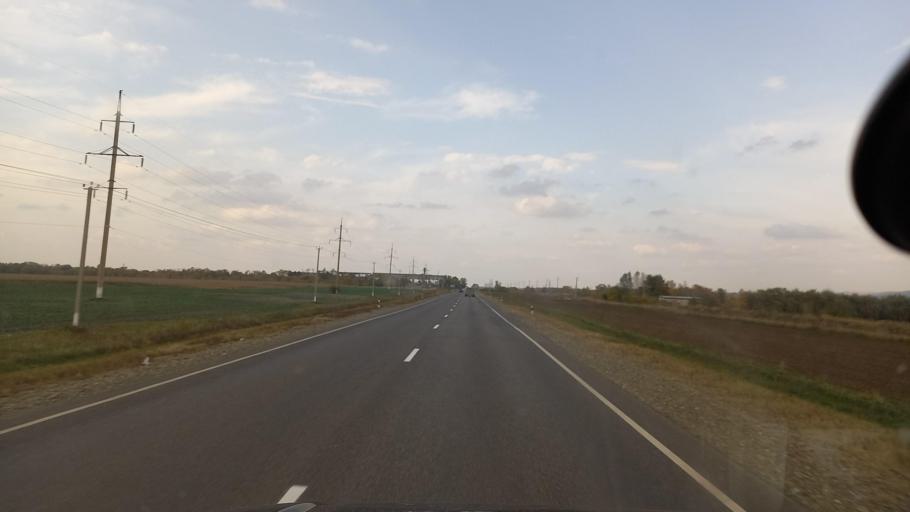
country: RU
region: Krasnodarskiy
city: Perepravnaya
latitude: 44.3686
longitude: 40.8287
